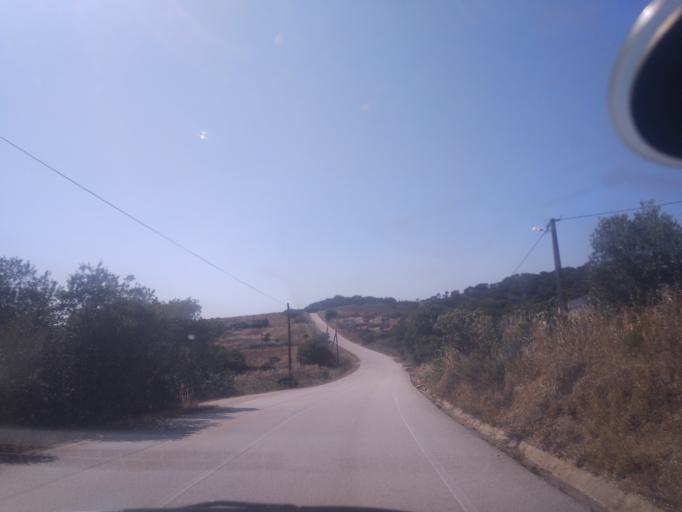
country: PT
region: Faro
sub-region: Aljezur
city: Aljezur
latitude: 37.2234
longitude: -8.8078
